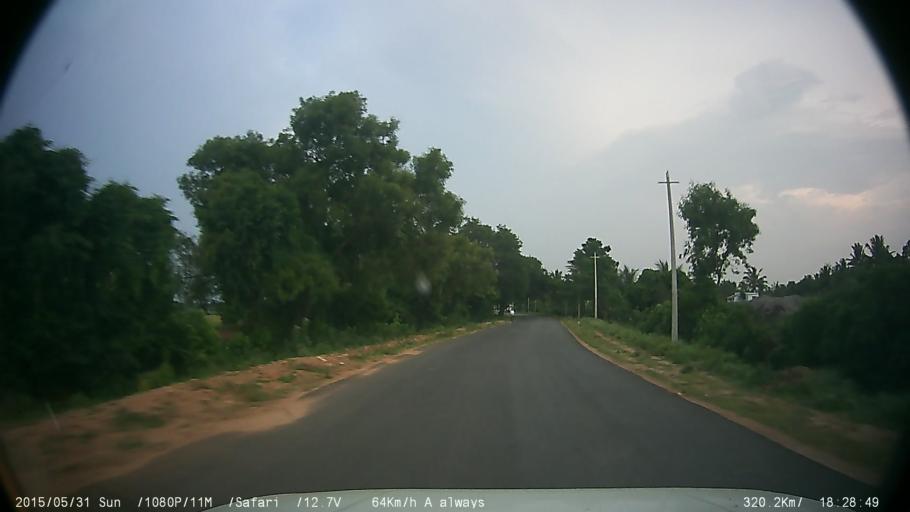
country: IN
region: Karnataka
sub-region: Mysore
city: Nanjangud
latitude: 12.1221
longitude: 76.7258
